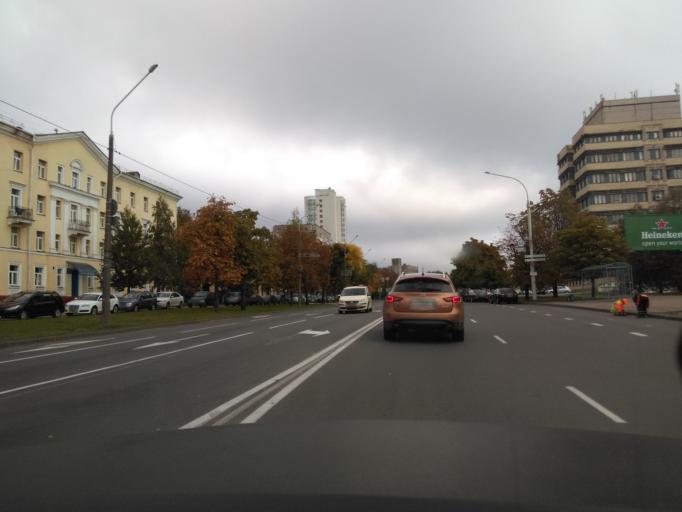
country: BY
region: Minsk
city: Minsk
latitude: 53.9064
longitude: 27.5914
